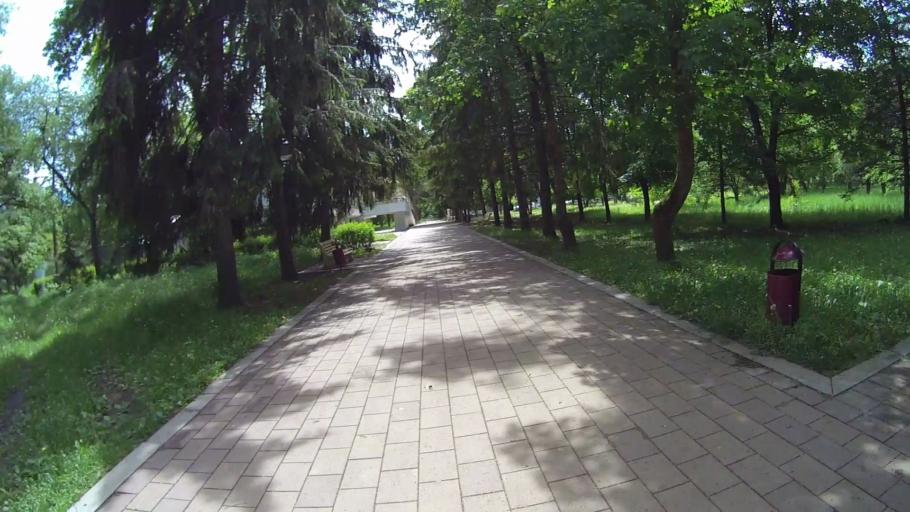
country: RU
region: Kabardino-Balkariya
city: Vol'nyy Aul
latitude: 43.4573
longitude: 43.5850
